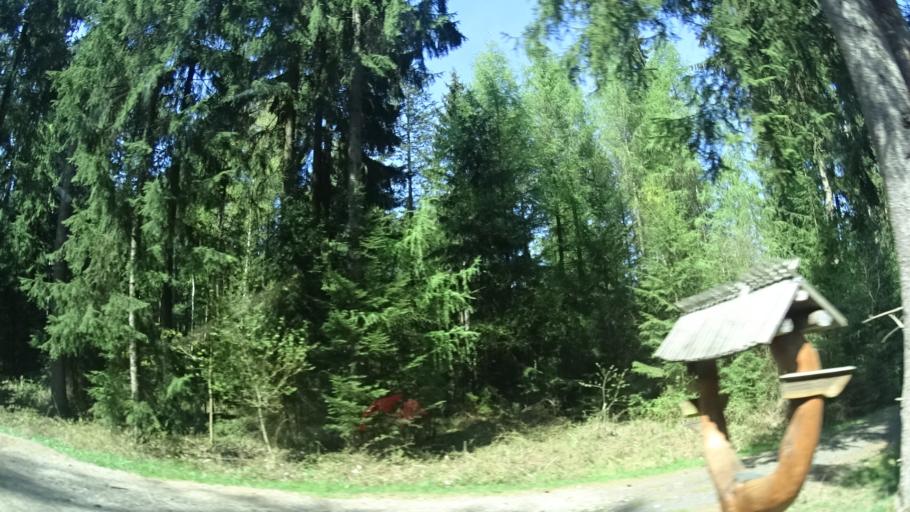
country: DE
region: Thuringia
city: Hildburghausen
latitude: 50.4502
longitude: 10.7720
